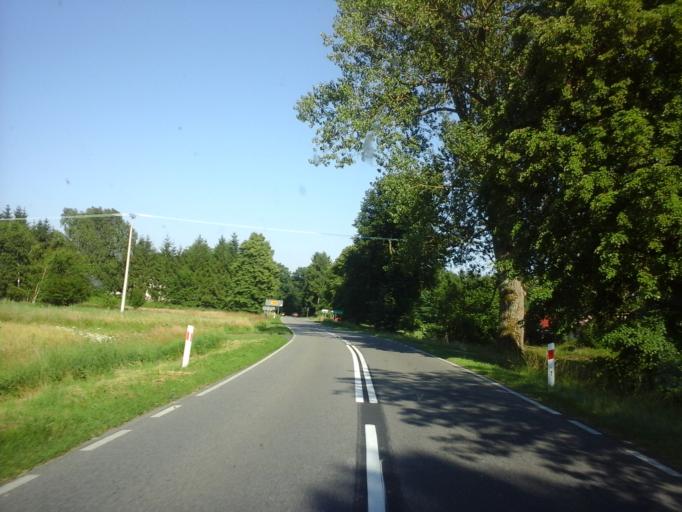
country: PL
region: West Pomeranian Voivodeship
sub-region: Powiat goleniowski
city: Nowogard
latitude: 53.6502
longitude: 15.2135
